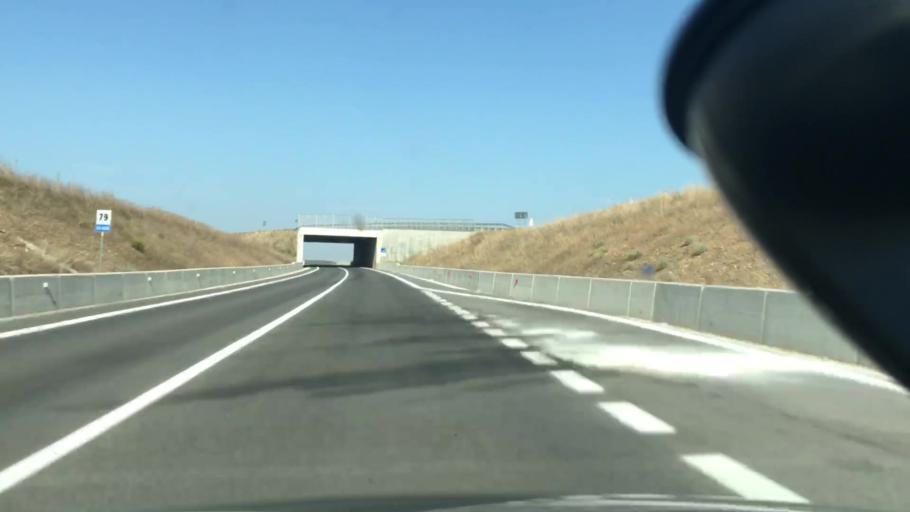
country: IT
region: Basilicate
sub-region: Provincia di Potenza
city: Palazzo San Gervasio
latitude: 40.9685
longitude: 16.0040
